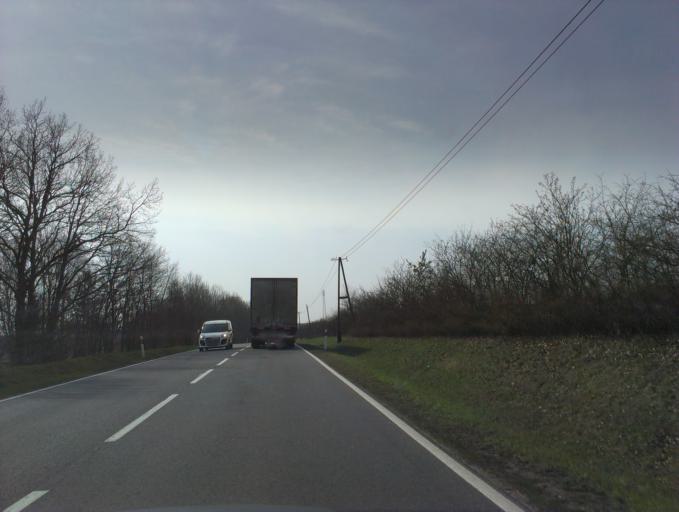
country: PL
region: Greater Poland Voivodeship
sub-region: Powiat zlotowski
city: Jastrowie
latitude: 53.3710
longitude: 16.7889
